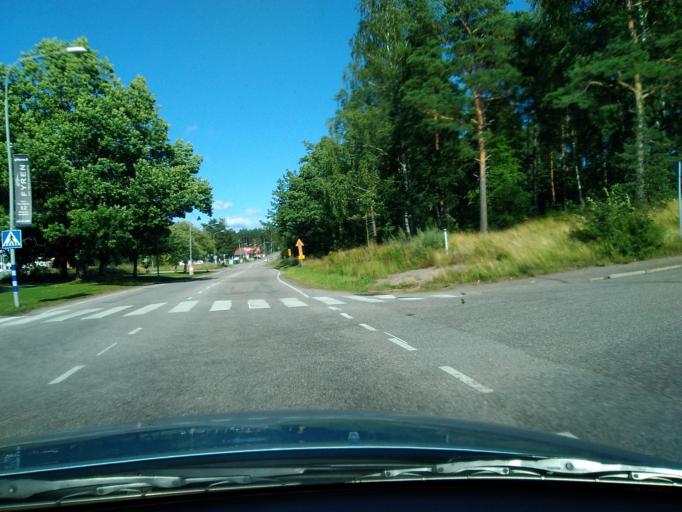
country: FI
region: Uusimaa
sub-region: Raaseporin
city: Ekenaes
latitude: 59.9803
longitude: 23.4530
